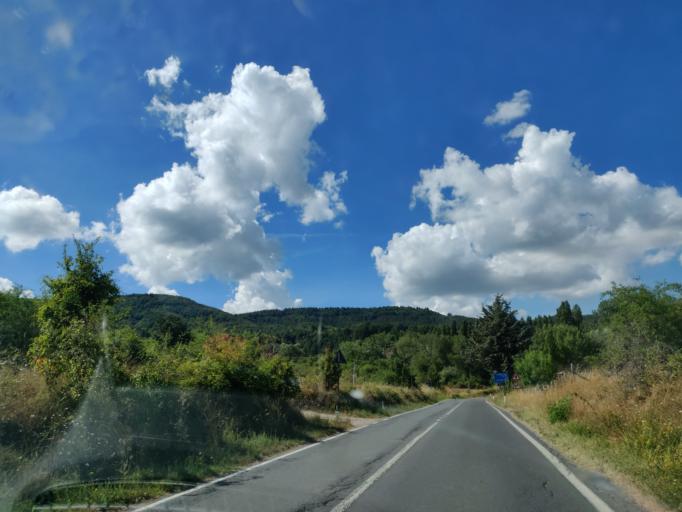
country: IT
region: Tuscany
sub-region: Provincia di Siena
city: Abbadia San Salvatore
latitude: 42.8988
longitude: 11.6682
